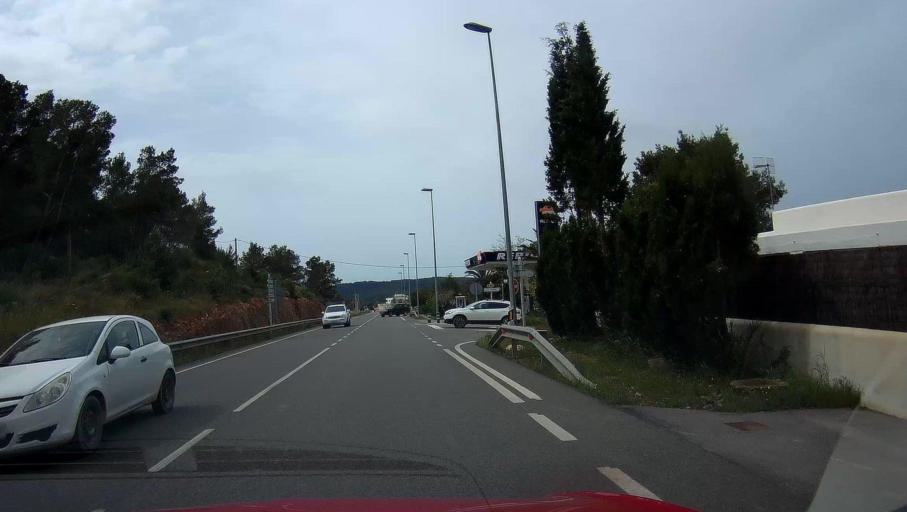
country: ES
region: Balearic Islands
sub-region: Illes Balears
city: Sant Joan de Labritja
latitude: 39.0707
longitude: 1.4967
